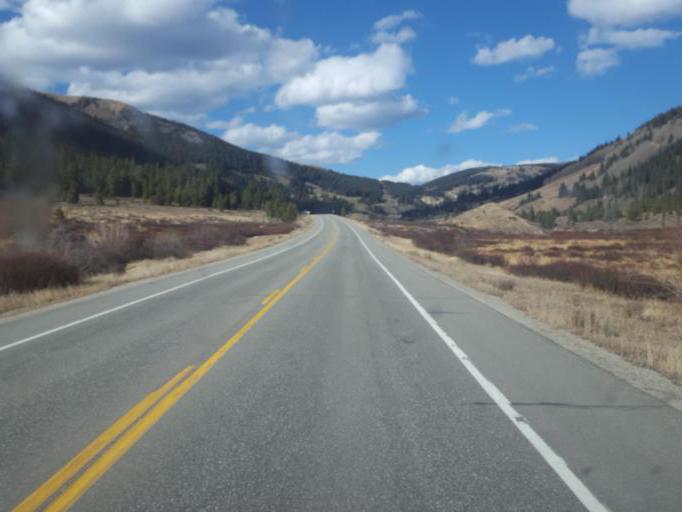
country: US
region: Colorado
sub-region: Lake County
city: Leadville
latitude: 39.3322
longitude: -106.2194
